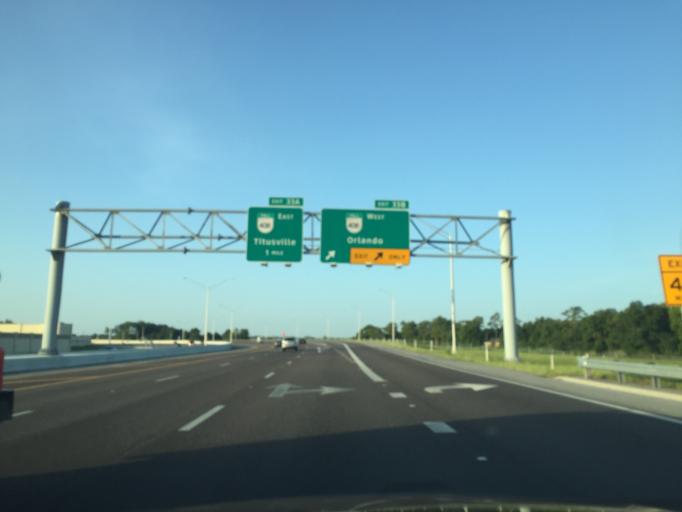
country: US
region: Florida
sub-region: Orange County
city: Union Park
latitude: 28.5613
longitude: -81.2681
